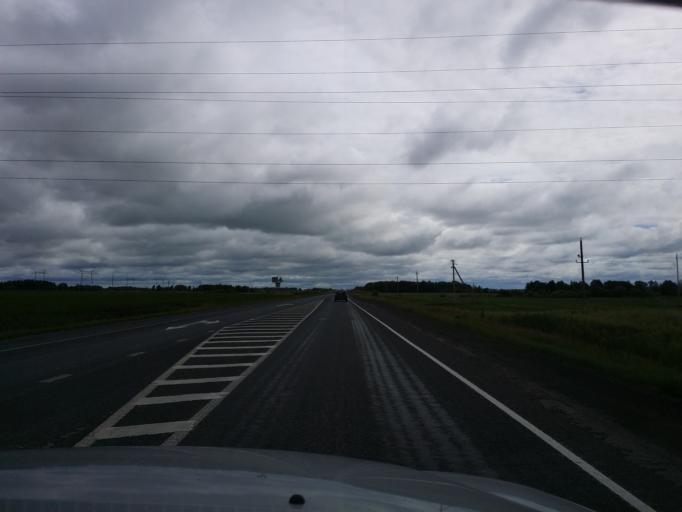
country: RU
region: Tjumen
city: Yarkovo
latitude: 57.1836
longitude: 66.5919
